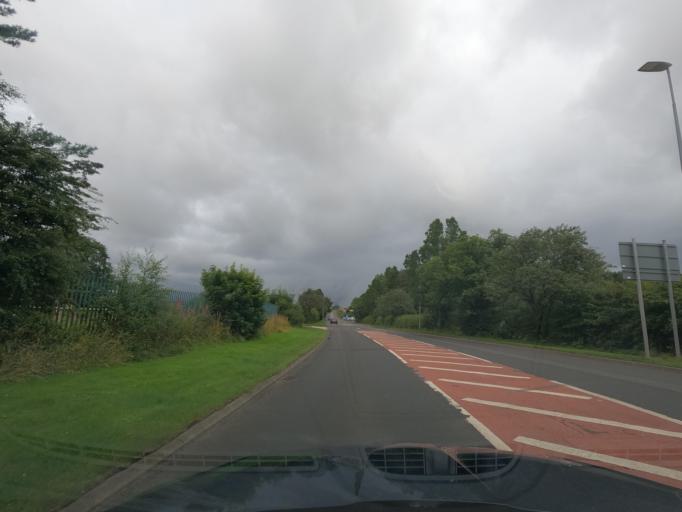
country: GB
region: England
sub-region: Northumberland
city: Berwick-Upon-Tweed
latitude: 55.7429
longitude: -1.9960
